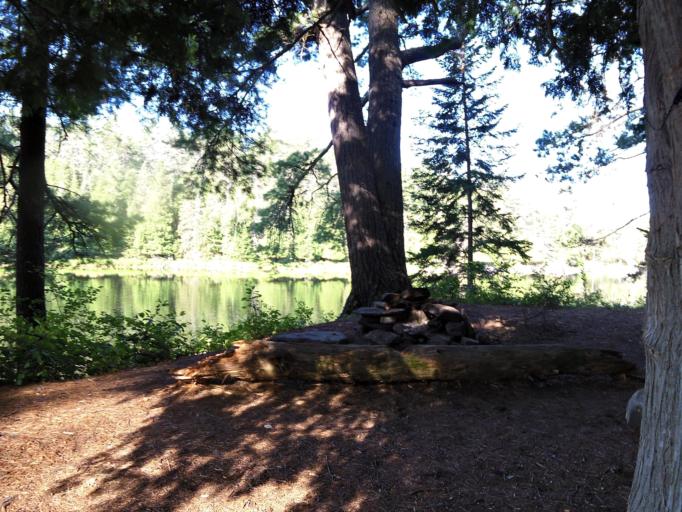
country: CA
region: Ontario
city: Pembroke
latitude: 45.2353
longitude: -77.2473
